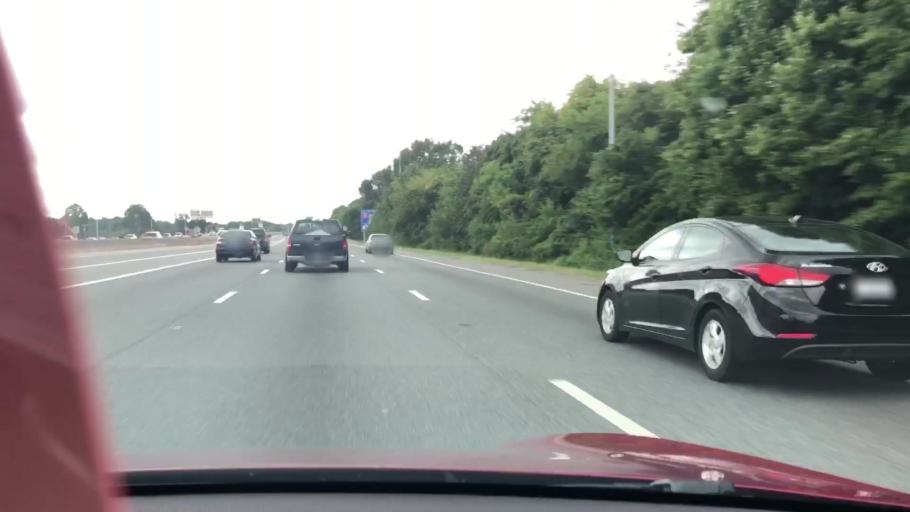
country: US
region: Virginia
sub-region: City of Chesapeake
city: Chesapeake
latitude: 36.8339
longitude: -76.1972
